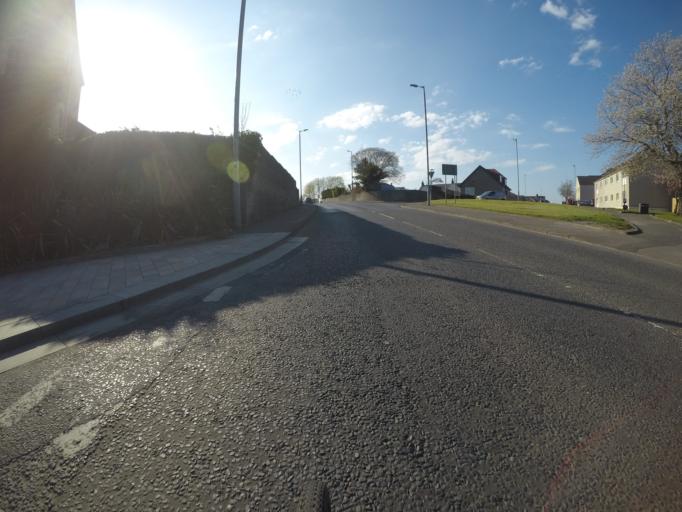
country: GB
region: Scotland
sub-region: North Ayrshire
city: Kilwinning
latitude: 55.6542
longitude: -4.6959
